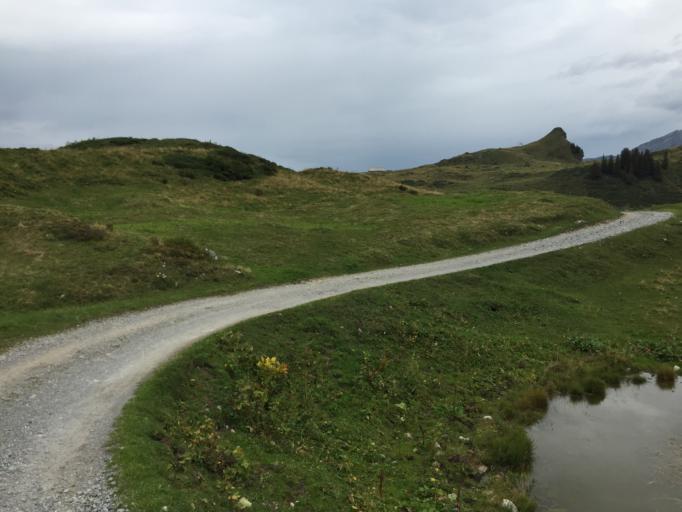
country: CH
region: Obwalden
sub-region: Obwalden
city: Engelberg
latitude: 46.7925
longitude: 8.3887
